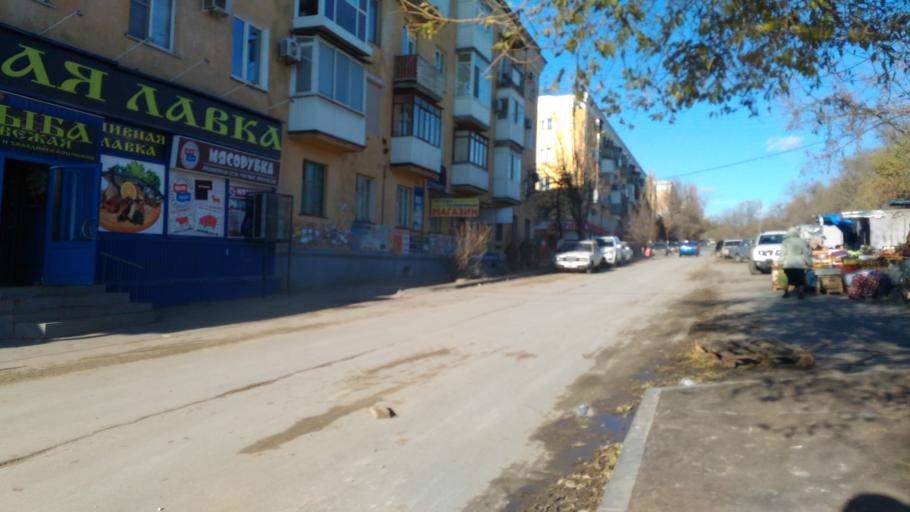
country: RU
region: Volgograd
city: Volgograd
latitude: 48.6594
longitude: 44.4376
